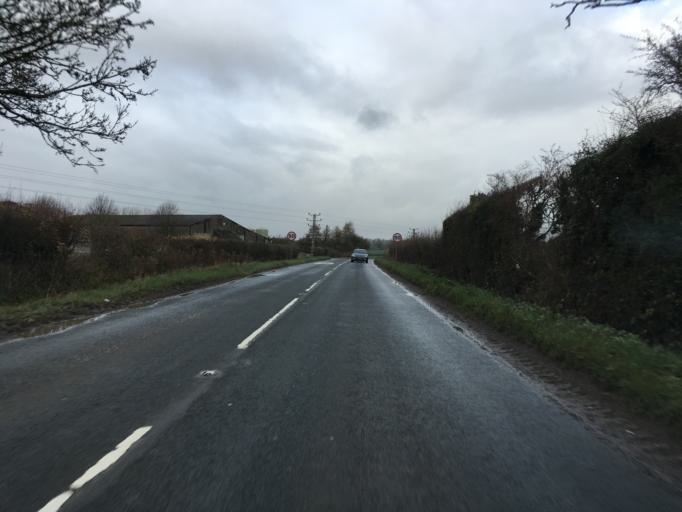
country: GB
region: England
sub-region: Wiltshire
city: Malmesbury
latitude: 51.6075
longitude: -2.1140
